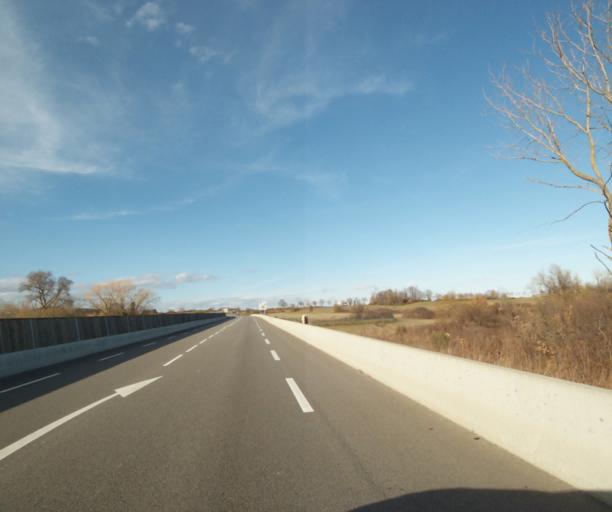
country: FR
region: Rhone-Alpes
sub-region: Departement de l'Ardeche
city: Davezieux
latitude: 45.2518
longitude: 4.7174
